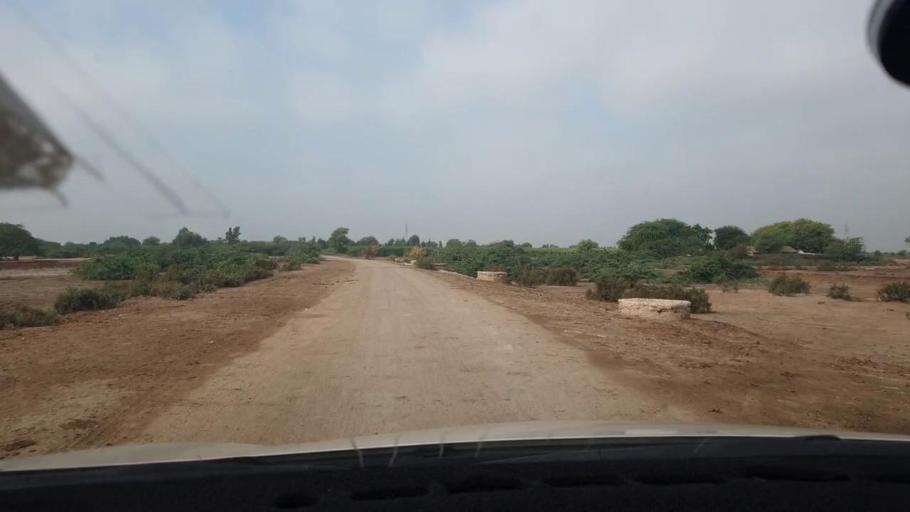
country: PK
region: Sindh
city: Sanghar
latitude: 26.0599
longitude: 68.9295
